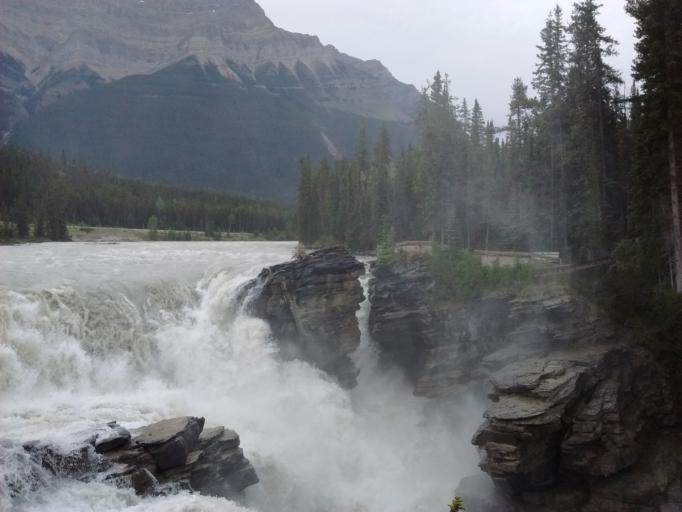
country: CA
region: Alberta
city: Jasper Park Lodge
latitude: 52.6646
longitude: -117.8841
